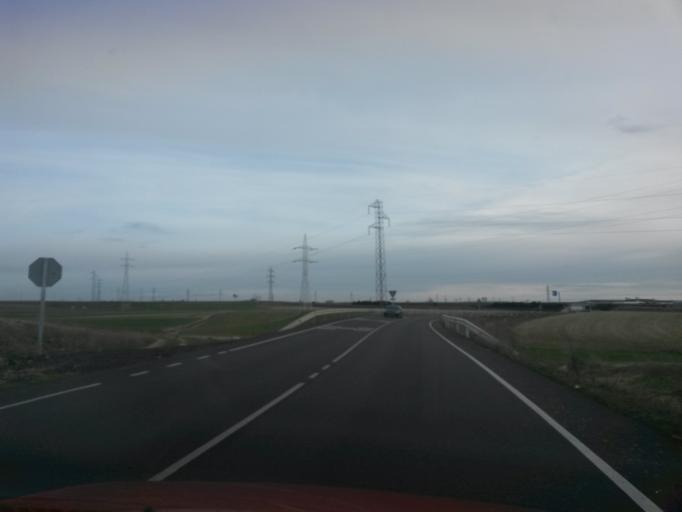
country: ES
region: Castille and Leon
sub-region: Provincia de Salamanca
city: Villares de la Reina
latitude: 41.0029
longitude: -5.6429
